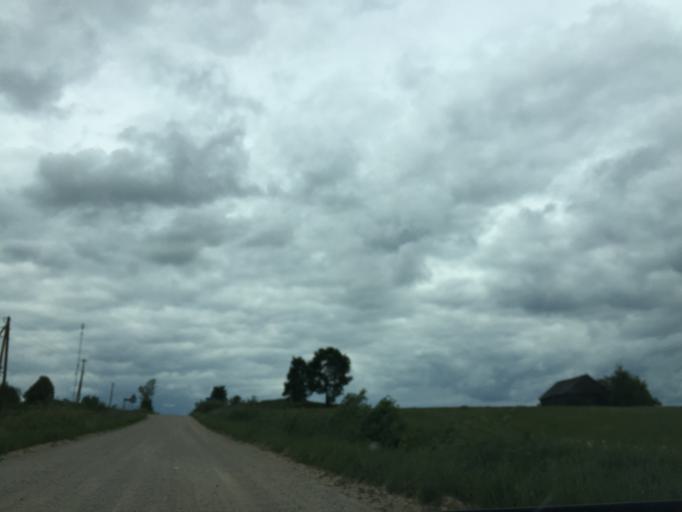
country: LV
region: Dagda
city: Dagda
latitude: 56.0126
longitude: 27.6014
